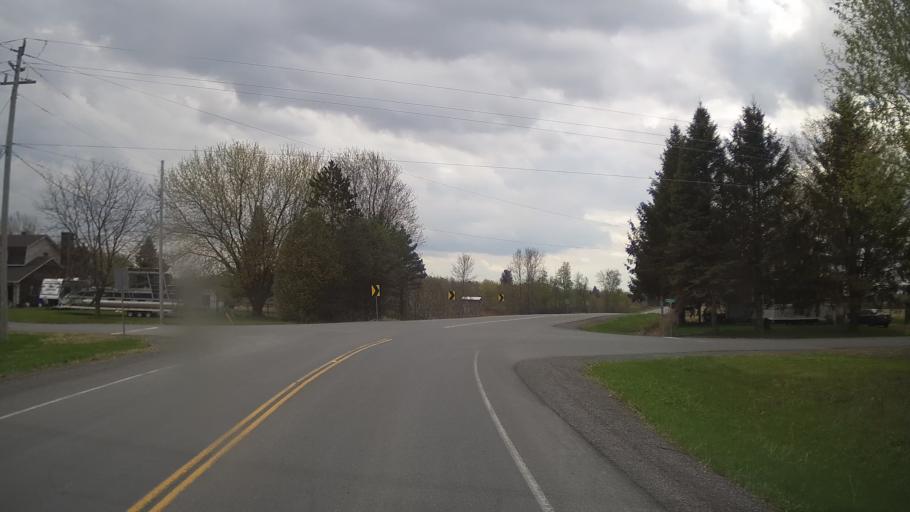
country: CA
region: Ontario
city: Hawkesbury
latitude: 45.5658
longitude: -74.5266
